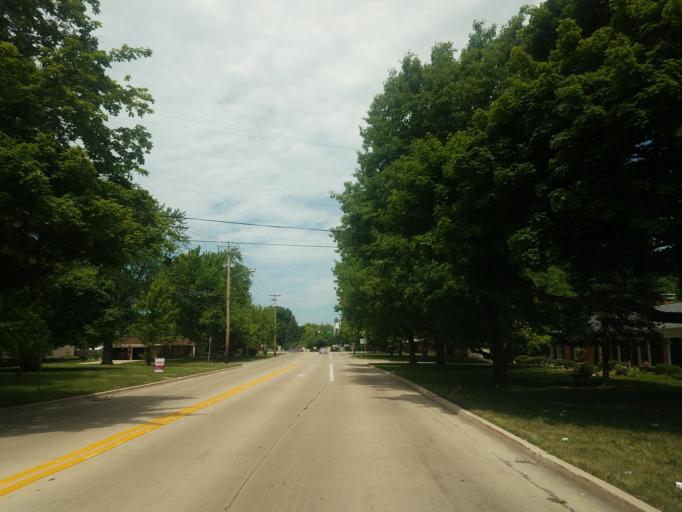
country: US
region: Illinois
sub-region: McLean County
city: Bloomington
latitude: 40.4926
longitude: -88.9634
